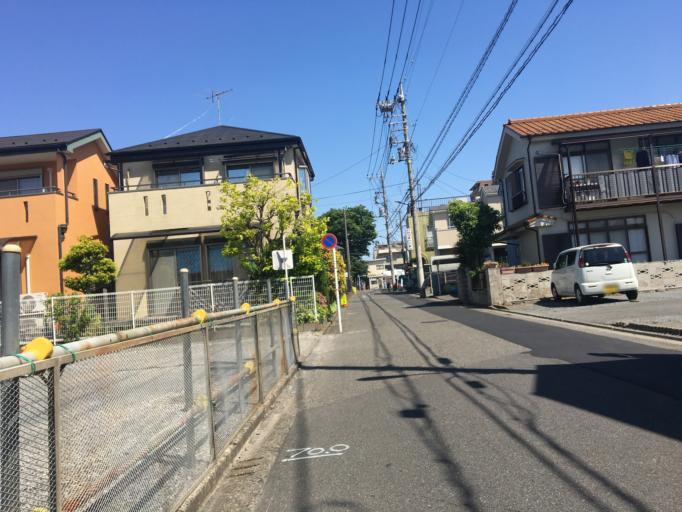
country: JP
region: Tokyo
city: Higashimurayama-shi
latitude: 35.7332
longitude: 139.4864
